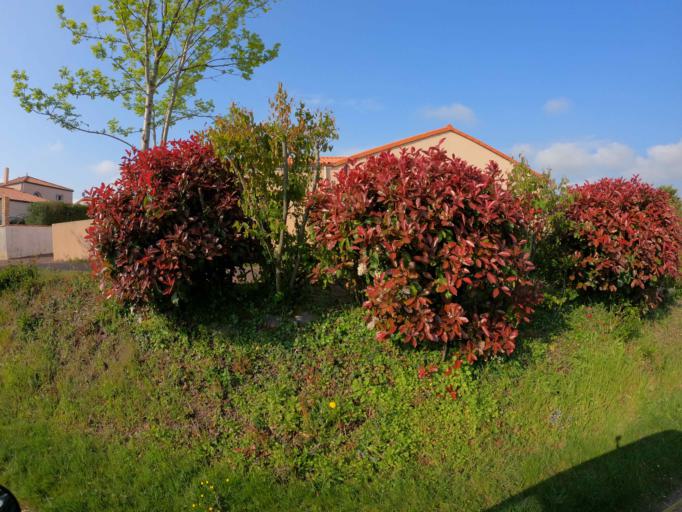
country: FR
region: Pays de la Loire
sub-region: Departement de Maine-et-Loire
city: La Romagne
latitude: 47.0590
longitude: -1.0172
